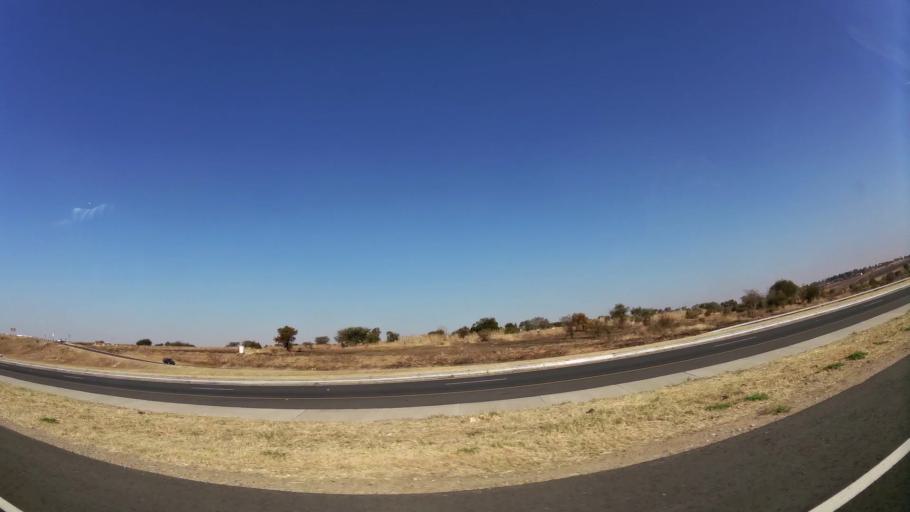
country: ZA
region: Gauteng
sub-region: West Rand District Municipality
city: Muldersdriseloop
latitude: -25.9849
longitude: 27.9228
